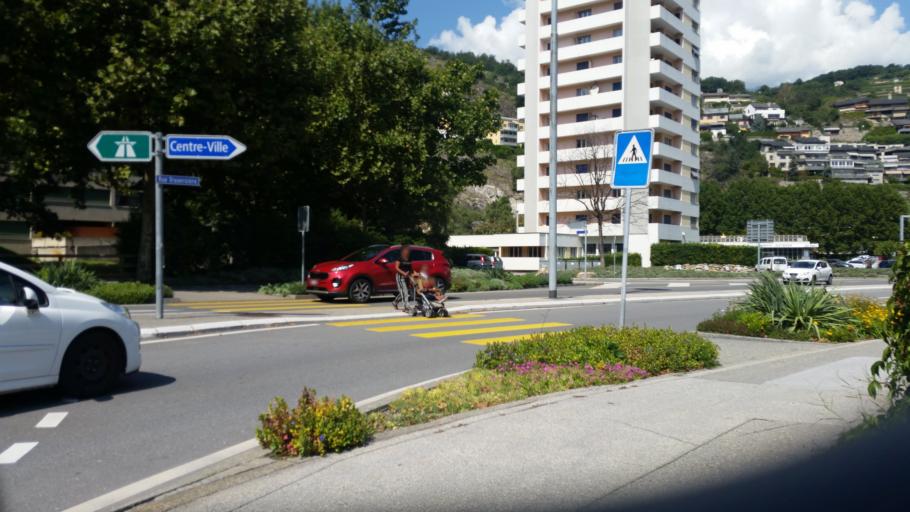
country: CH
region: Valais
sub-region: Sion District
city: Sitten
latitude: 46.2276
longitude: 7.3466
